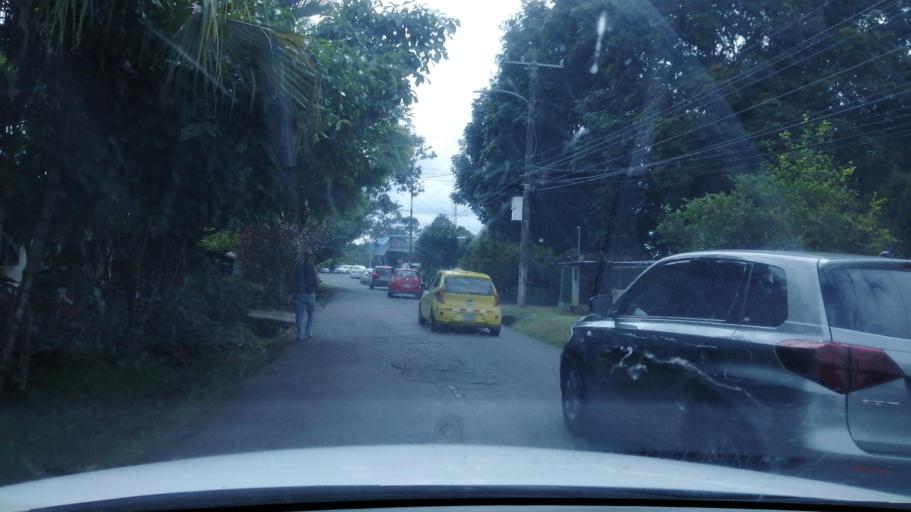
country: PA
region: Chiriqui
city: David
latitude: 8.4466
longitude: -82.4290
